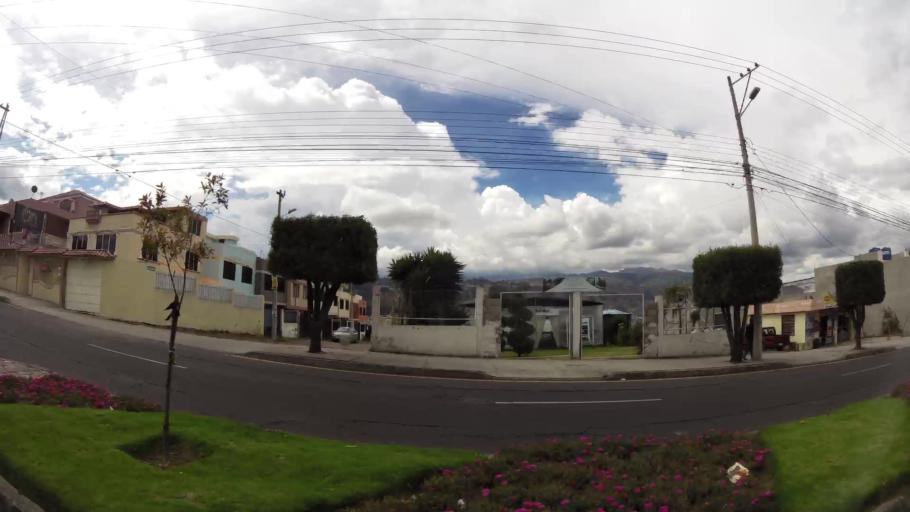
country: EC
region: Tungurahua
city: Ambato
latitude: -1.2666
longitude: -78.6313
